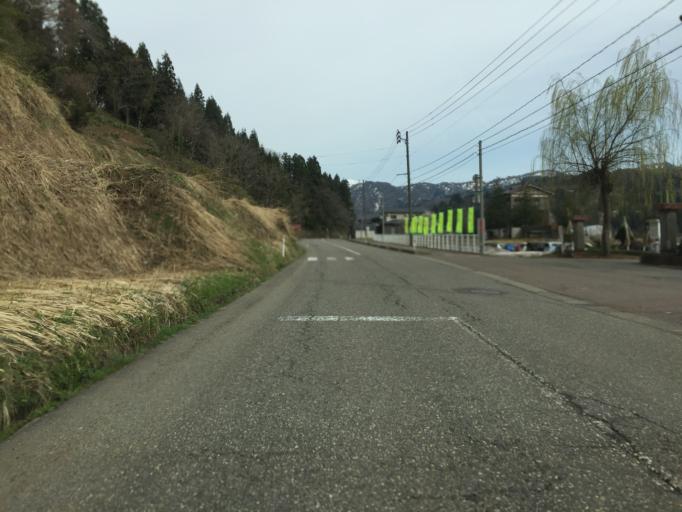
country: JP
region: Niigata
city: Tochio-honcho
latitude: 37.4478
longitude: 139.0190
